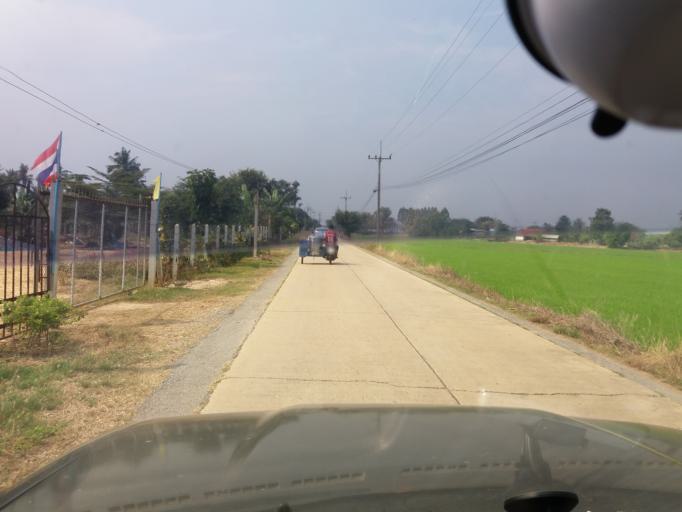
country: TH
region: Suphan Buri
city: Doem Bang Nang Buat
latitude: 14.8926
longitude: 100.1883
